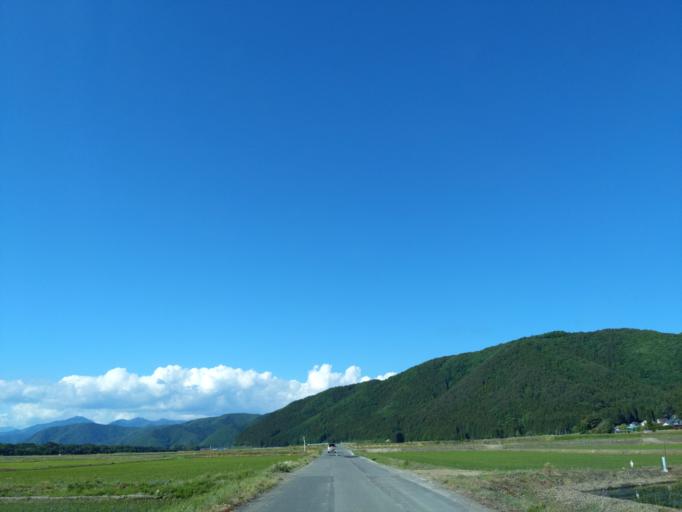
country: JP
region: Fukushima
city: Inawashiro
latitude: 37.4215
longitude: 140.1387
